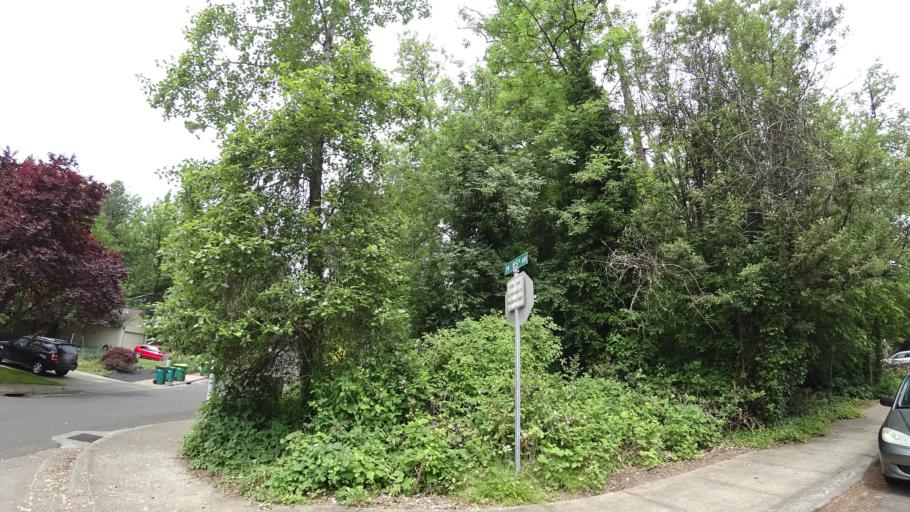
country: US
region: Oregon
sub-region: Washington County
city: Garden Home-Whitford
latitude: 45.4592
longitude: -122.7637
